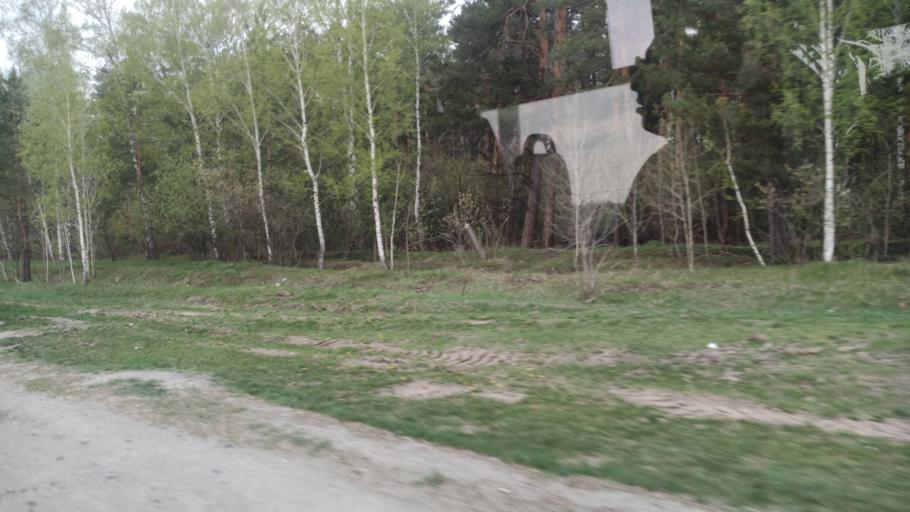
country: RU
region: Altai Krai
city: Yuzhnyy
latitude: 53.2635
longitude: 83.7066
